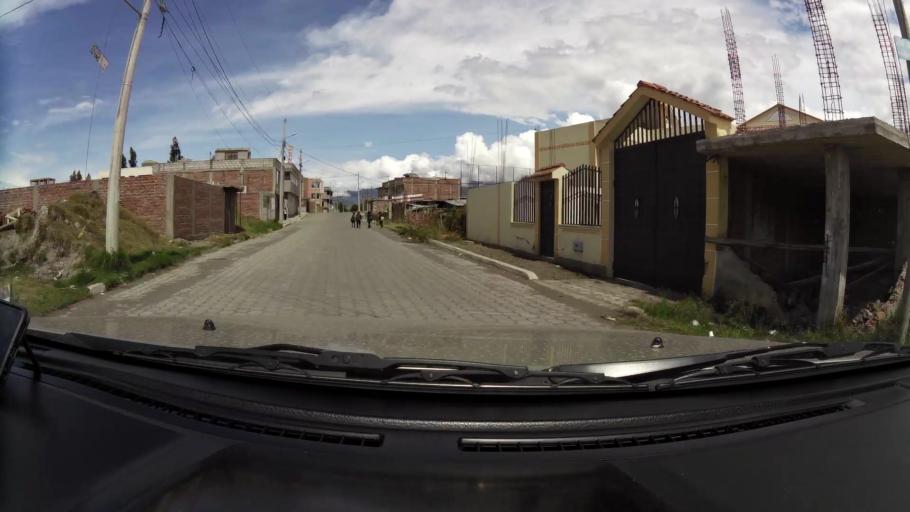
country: EC
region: Chimborazo
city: Riobamba
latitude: -1.6568
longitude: -78.6396
